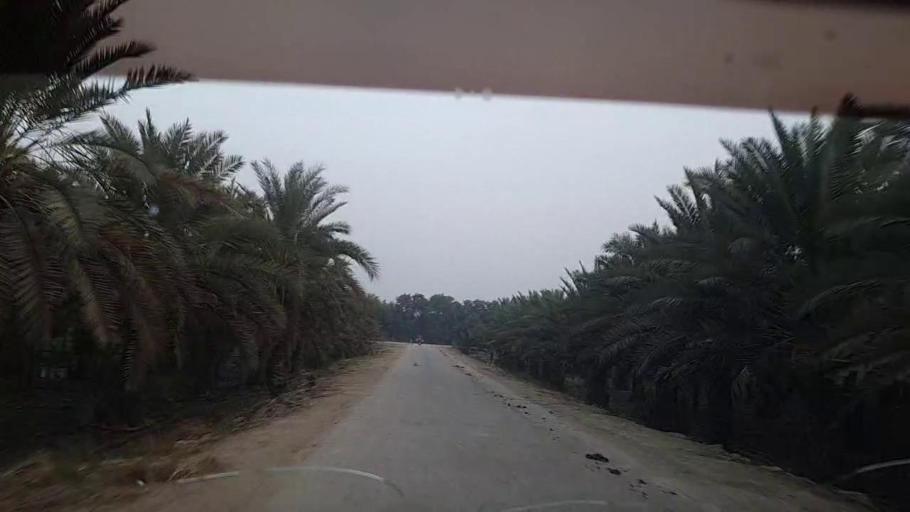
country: PK
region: Sindh
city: Khairpur
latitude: 27.5739
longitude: 68.7249
